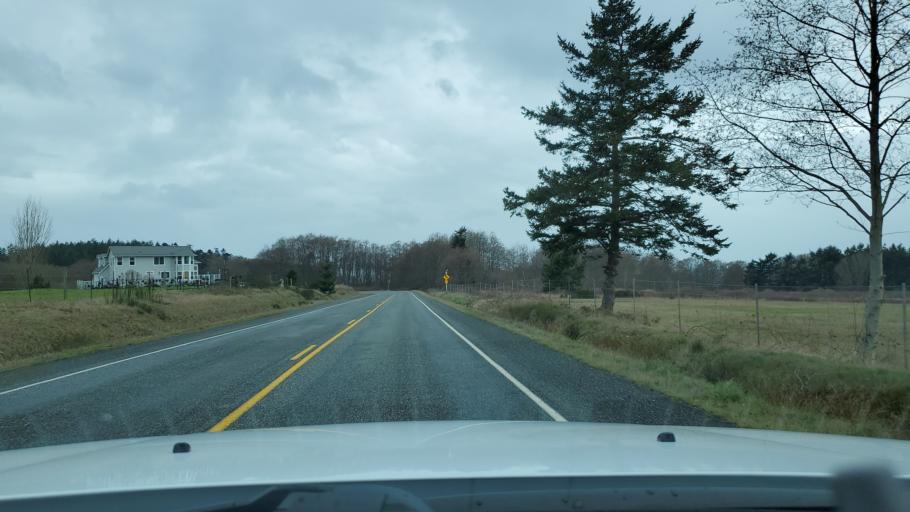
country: US
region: Washington
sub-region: Island County
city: Ault Field
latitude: 48.3114
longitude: -122.6983
